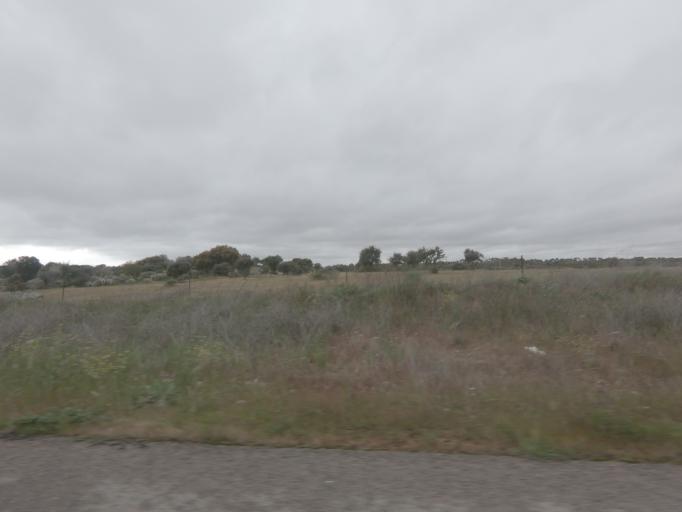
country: ES
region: Extremadura
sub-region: Provincia de Caceres
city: Caceres
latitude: 39.4079
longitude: -6.4180
